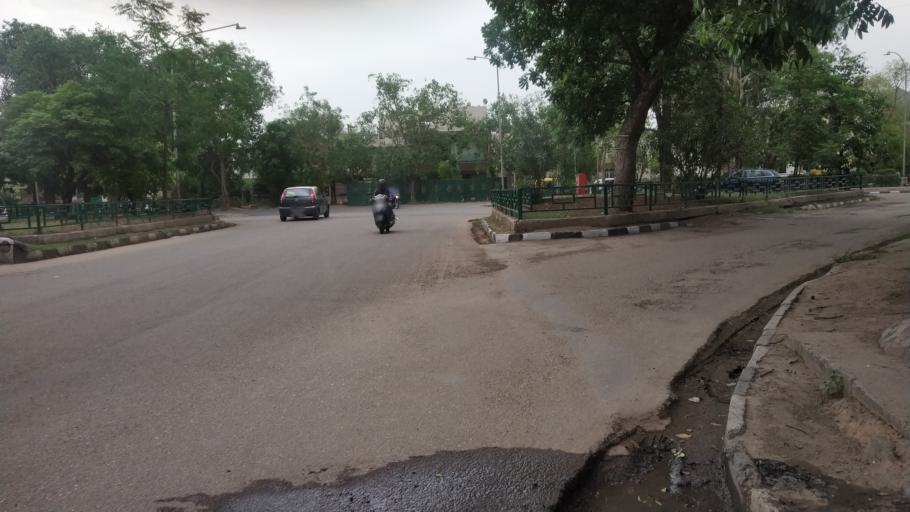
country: IN
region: Punjab
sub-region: Ajitgarh
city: Mohali
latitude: 30.6947
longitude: 76.7169
